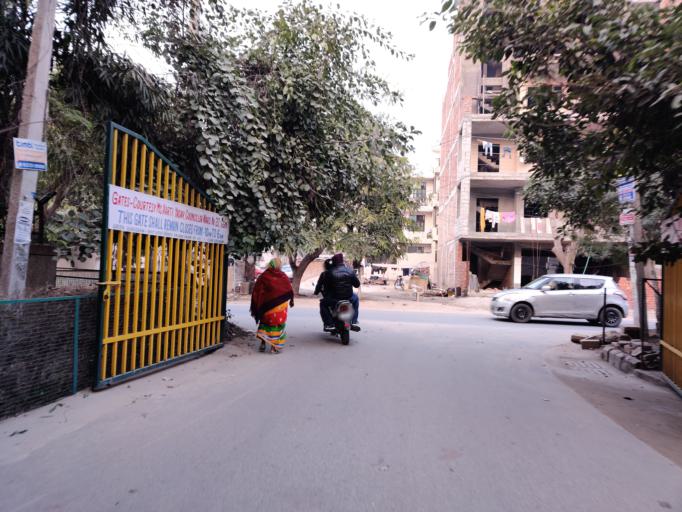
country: IN
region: Haryana
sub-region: Gurgaon
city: Gurgaon
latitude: 28.4431
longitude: 77.0640
